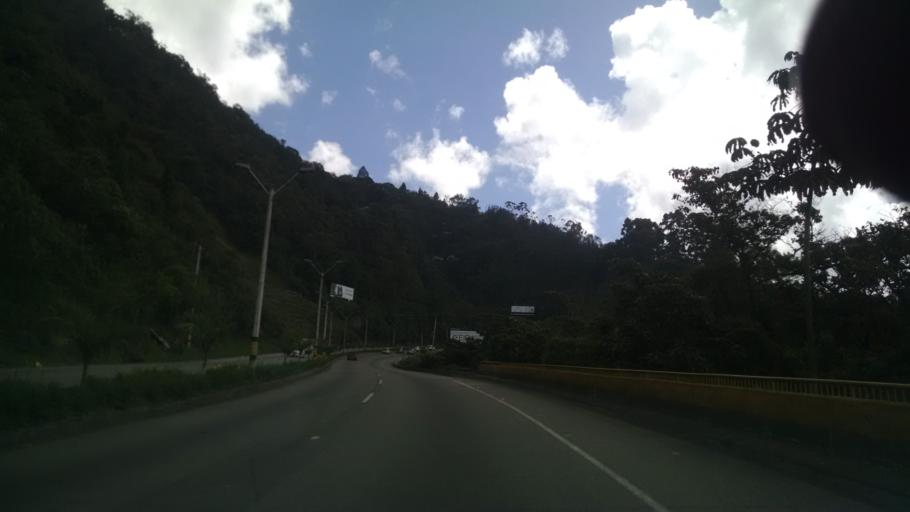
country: CO
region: Antioquia
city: Envigado
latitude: 6.1630
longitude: -75.5457
